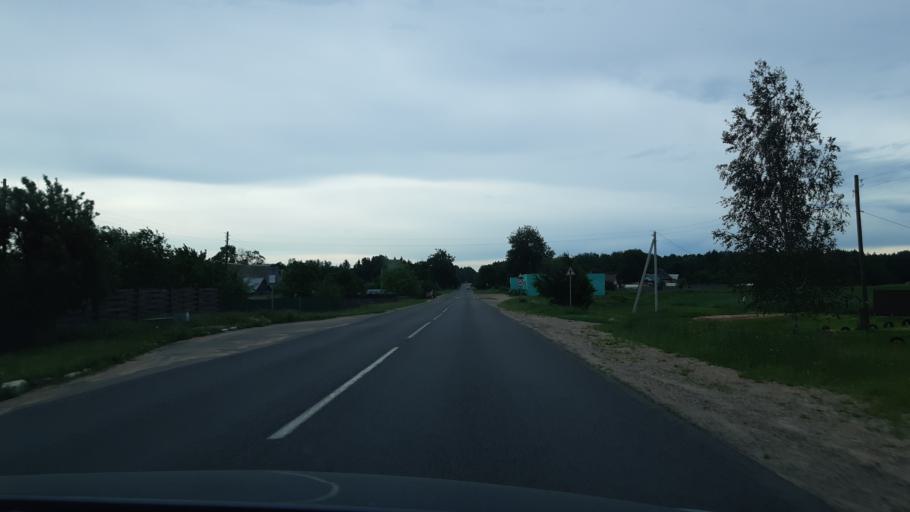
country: BY
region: Minsk
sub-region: Smalyavitski Rayon
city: Oktjabr'skij
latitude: 54.1113
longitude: 28.1820
